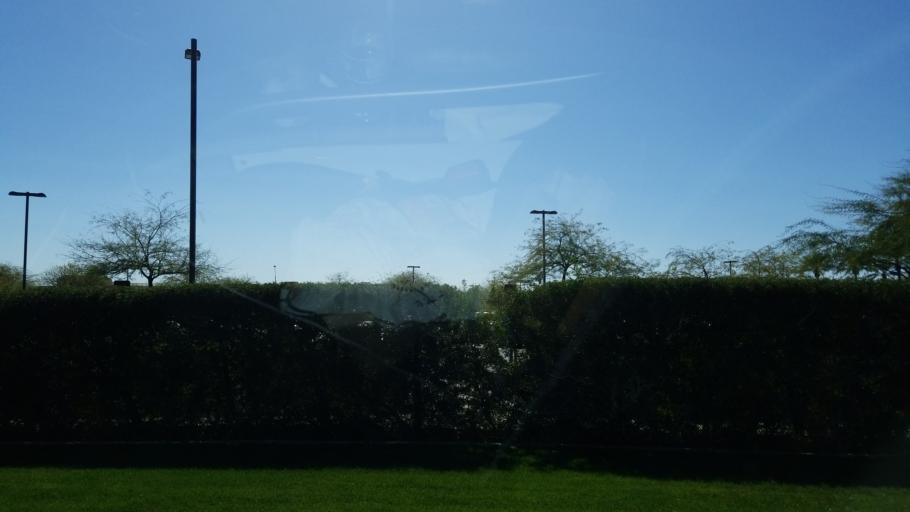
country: US
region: Arizona
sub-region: Maricopa County
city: Paradise Valley
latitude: 33.6244
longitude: -111.9322
